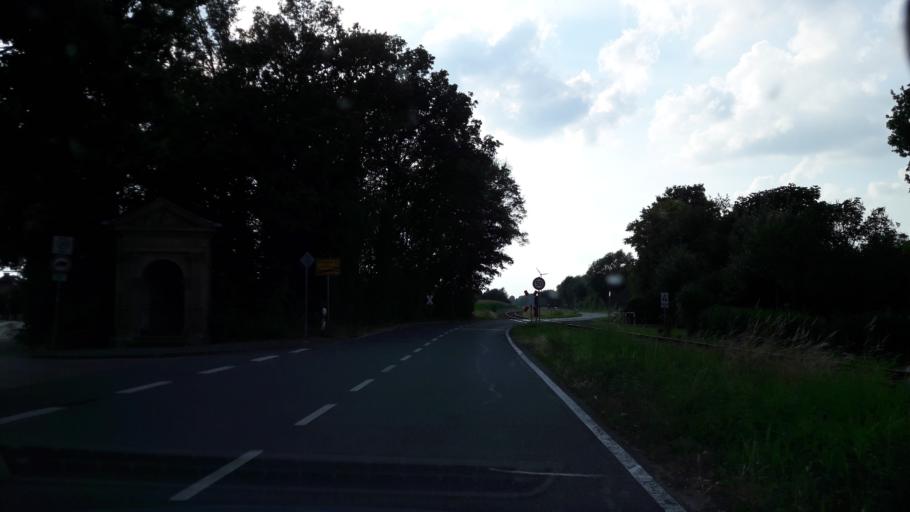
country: DE
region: North Rhine-Westphalia
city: Sendenhorst
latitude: 51.8495
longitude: 7.8223
